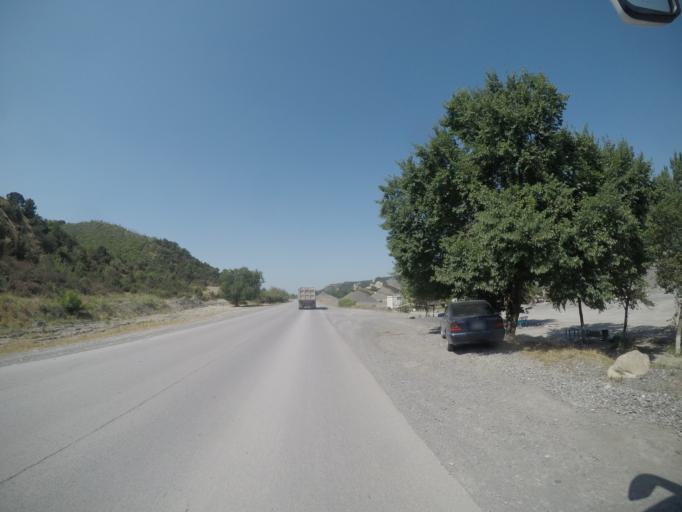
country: AZ
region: Agdas
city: Agdas
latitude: 40.7295
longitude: 47.5700
